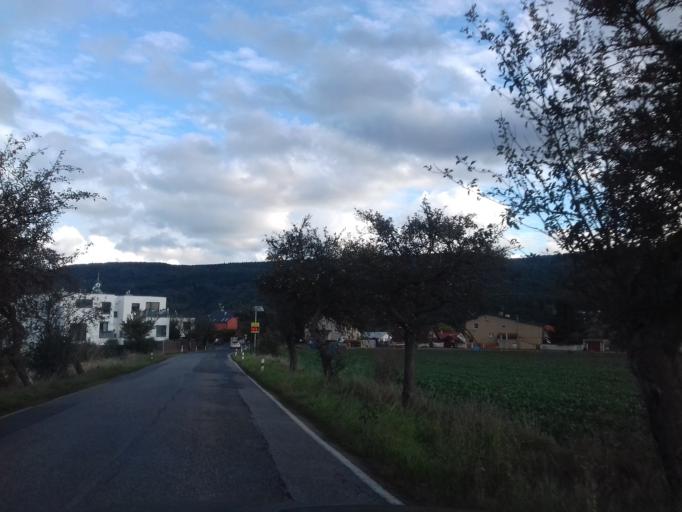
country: CZ
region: Central Bohemia
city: Revnice
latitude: 49.9235
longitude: 14.2483
